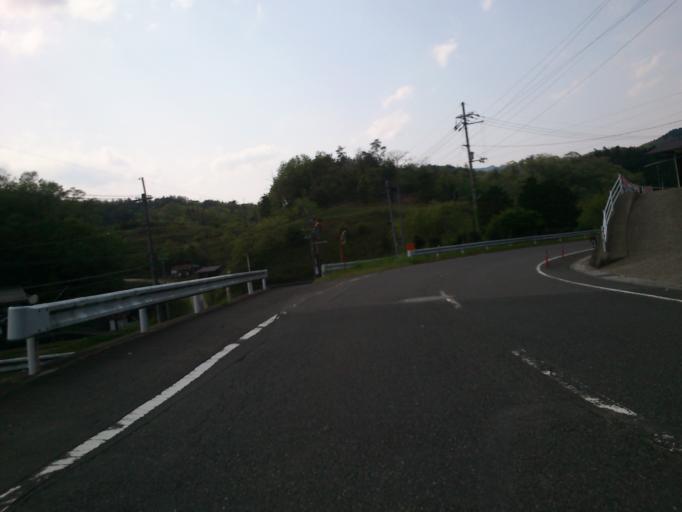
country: JP
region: Kyoto
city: Fukuchiyama
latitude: 35.3182
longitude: 134.9581
